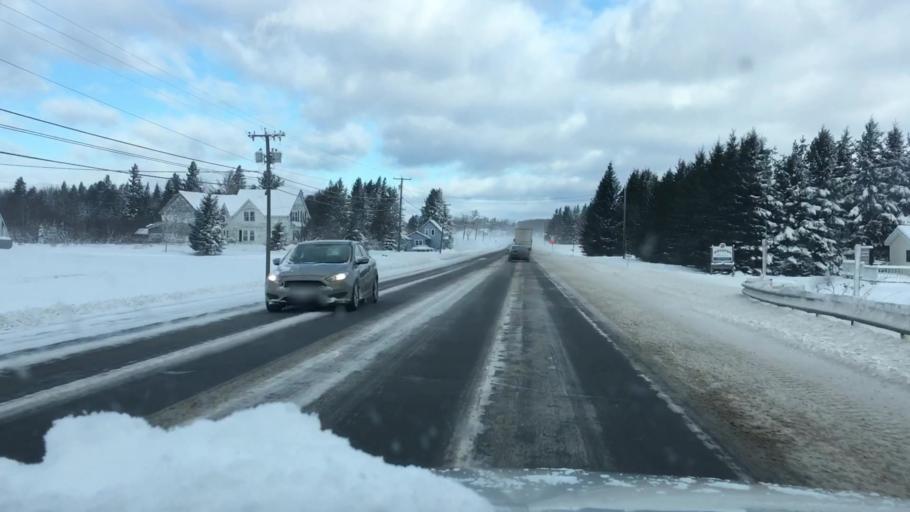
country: US
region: Maine
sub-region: Aroostook County
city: Caribou
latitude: 46.8049
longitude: -67.9932
